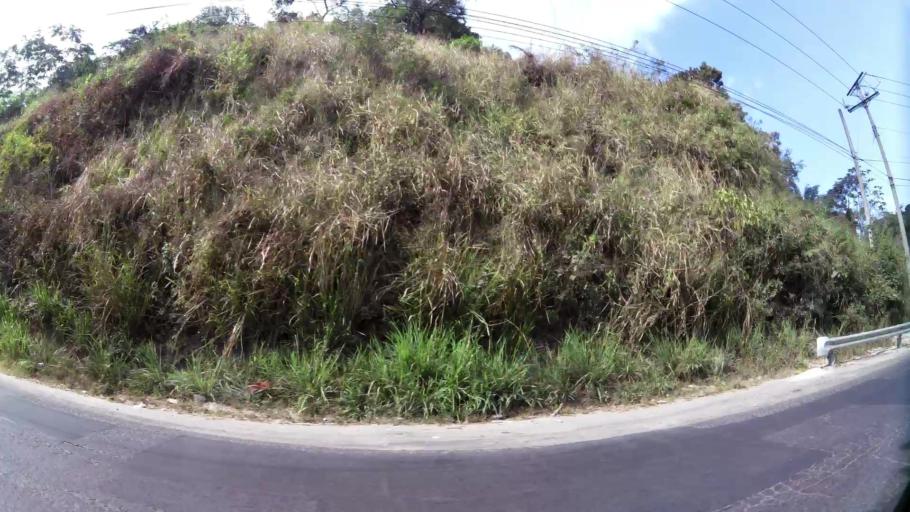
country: SV
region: San Salvador
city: Delgado
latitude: 13.7202
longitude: -89.1604
